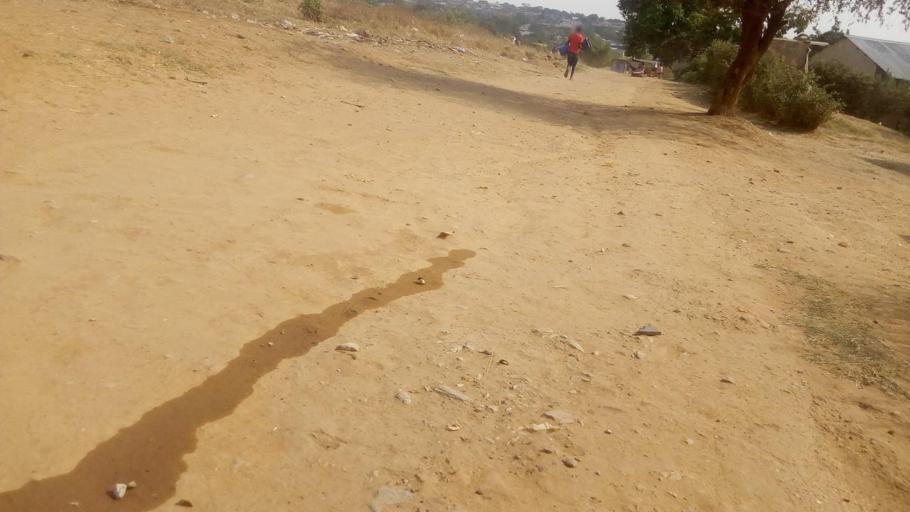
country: ZM
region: Lusaka
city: Lusaka
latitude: -15.3618
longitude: 28.3048
